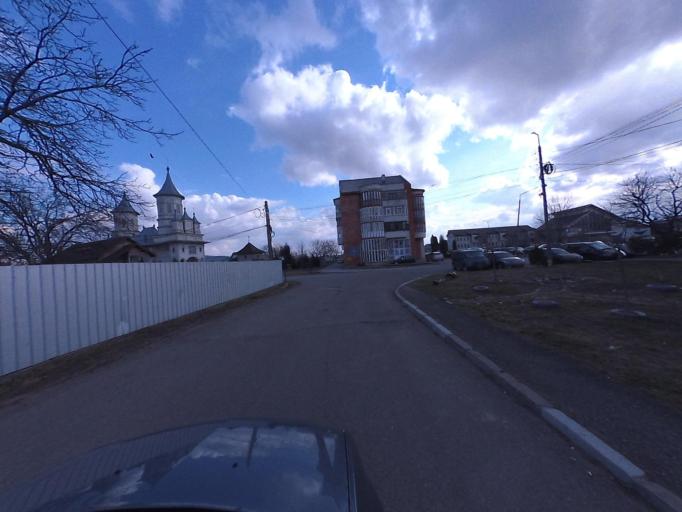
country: RO
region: Neamt
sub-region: Oras Targu Neamt
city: Targu Neamt
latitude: 47.2015
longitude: 26.3771
